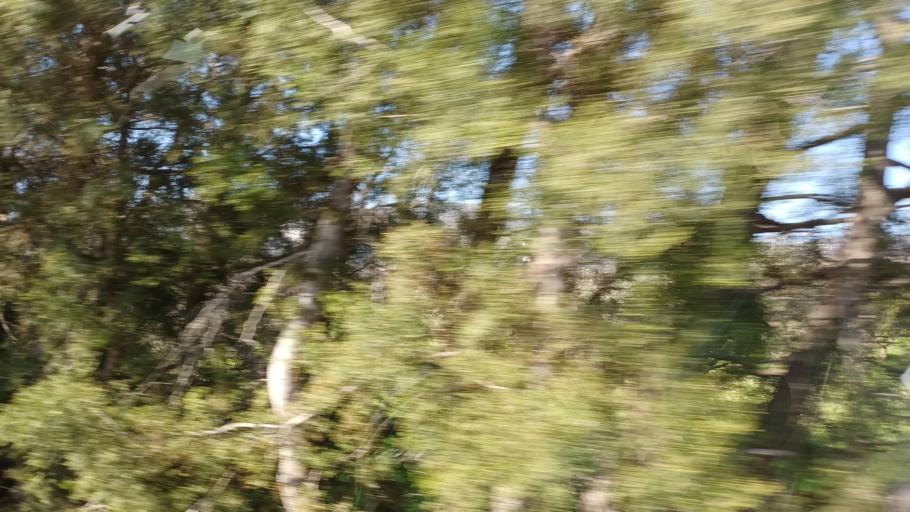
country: CY
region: Limassol
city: Pelendri
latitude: 34.8145
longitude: 32.9123
